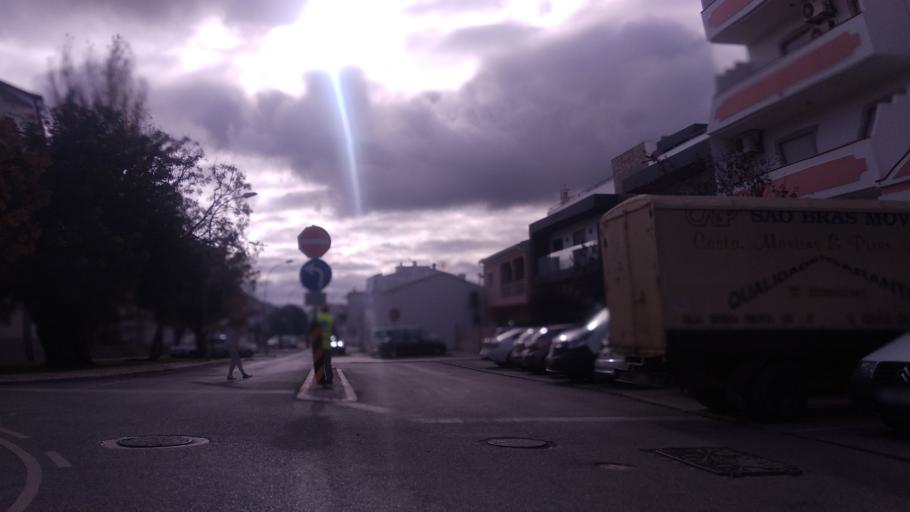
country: PT
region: Faro
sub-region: Sao Bras de Alportel
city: Sao Bras de Alportel
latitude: 37.1558
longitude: -7.8916
